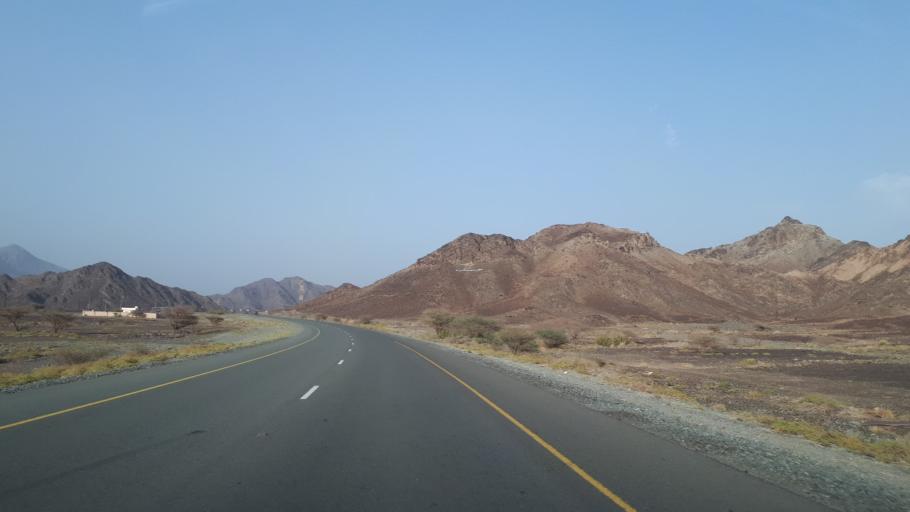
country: OM
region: Az Zahirah
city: Yanqul
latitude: 23.4824
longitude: 56.8086
